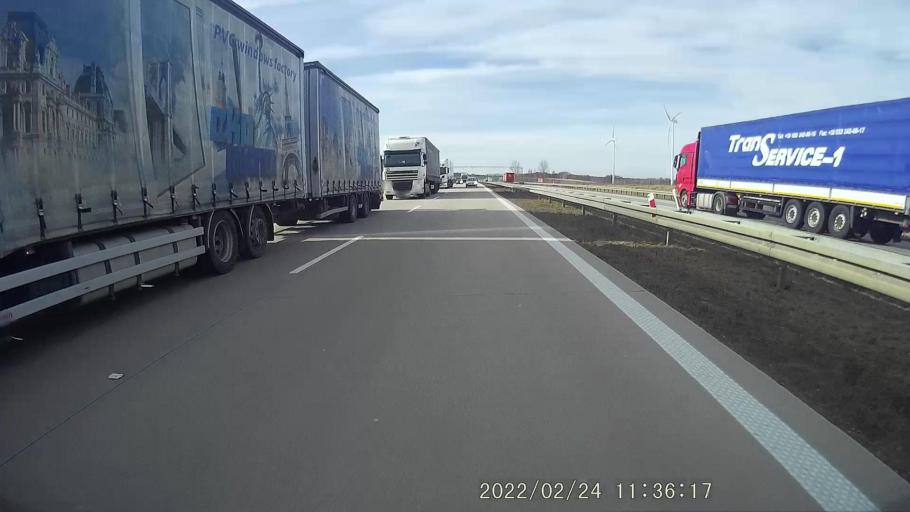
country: PL
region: Lower Silesian Voivodeship
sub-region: Powiat polkowicki
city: Przemkow
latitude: 51.5228
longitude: 15.8043
